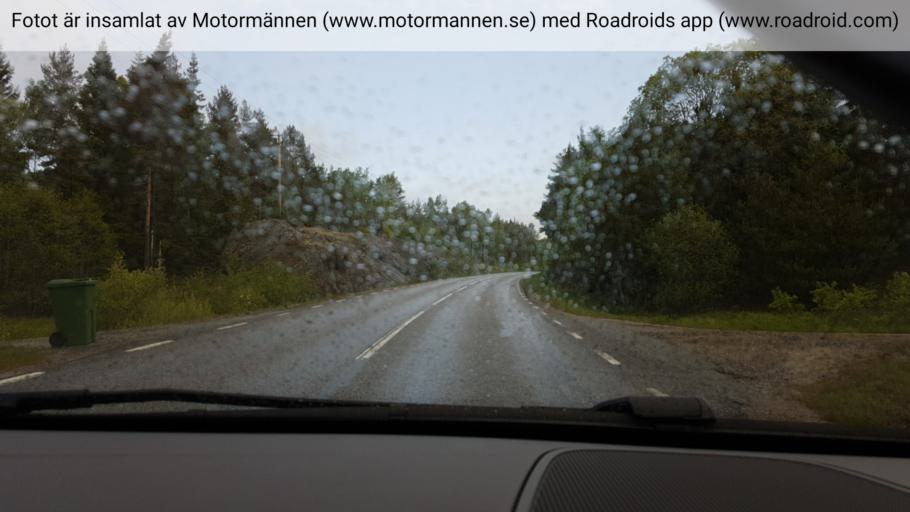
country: SE
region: Stockholm
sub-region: Nynashamns Kommun
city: Nynashamn
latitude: 58.9541
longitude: 17.9978
